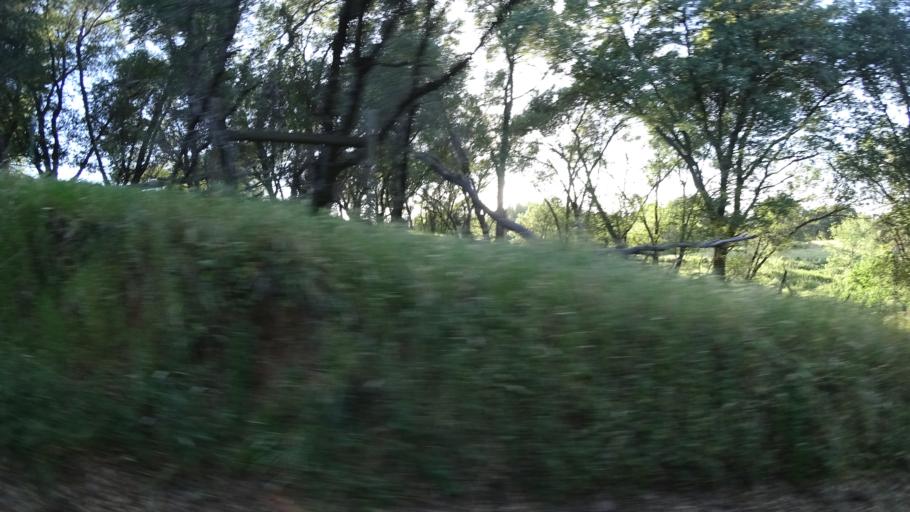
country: US
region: California
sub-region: Placer County
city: Lincoln
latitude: 38.9171
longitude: -121.2238
